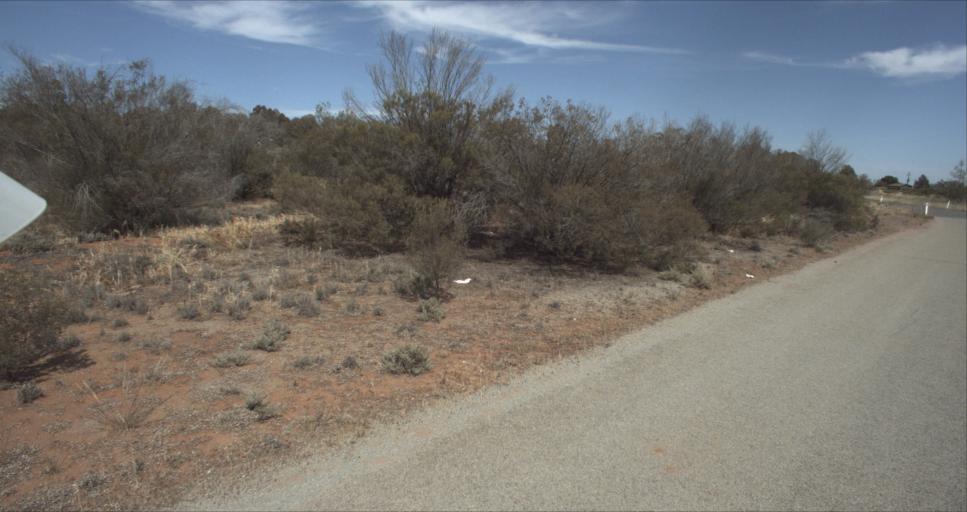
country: AU
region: New South Wales
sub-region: Leeton
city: Leeton
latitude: -34.5717
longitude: 146.4517
